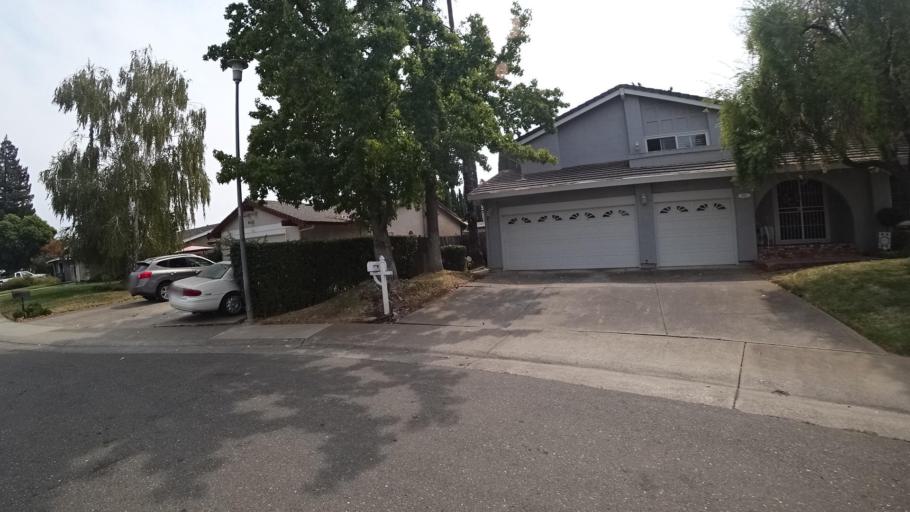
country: US
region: California
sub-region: Sacramento County
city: Elk Grove
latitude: 38.4214
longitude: -121.3895
